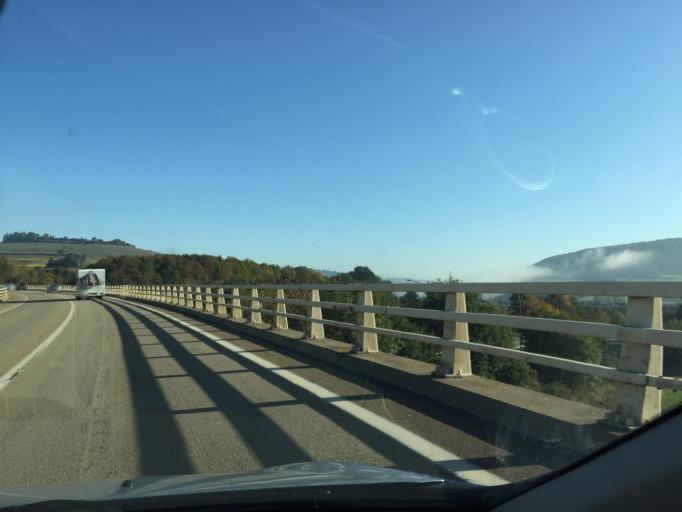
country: LU
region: Diekirch
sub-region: Canton de Diekirch
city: Ettelbruck
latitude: 49.8491
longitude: 6.1203
